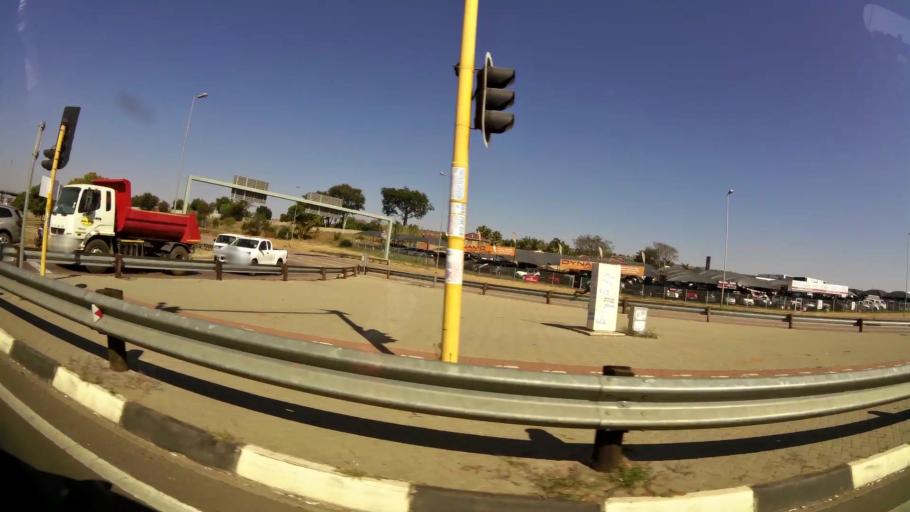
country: ZA
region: Gauteng
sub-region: City of Tshwane Metropolitan Municipality
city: Pretoria
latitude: -25.6842
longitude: 28.2790
